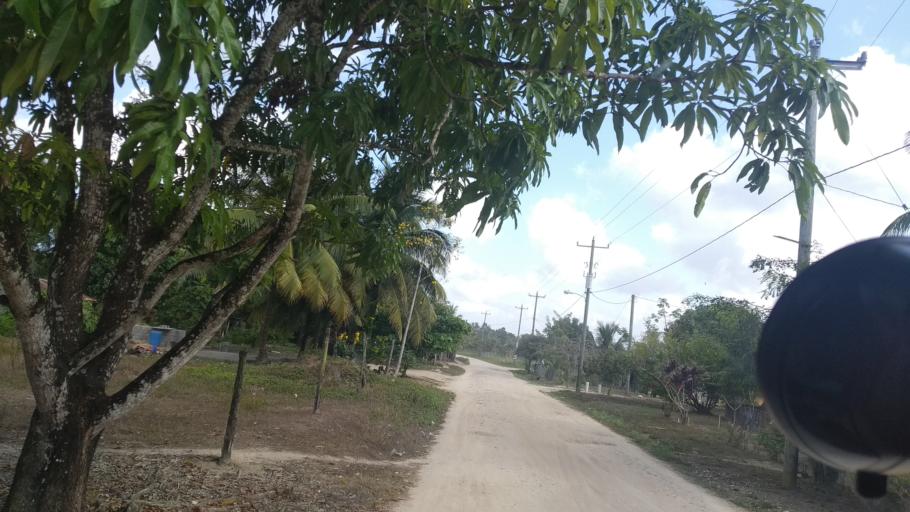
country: BZ
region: Stann Creek
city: Placencia
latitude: 16.4715
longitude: -88.6243
